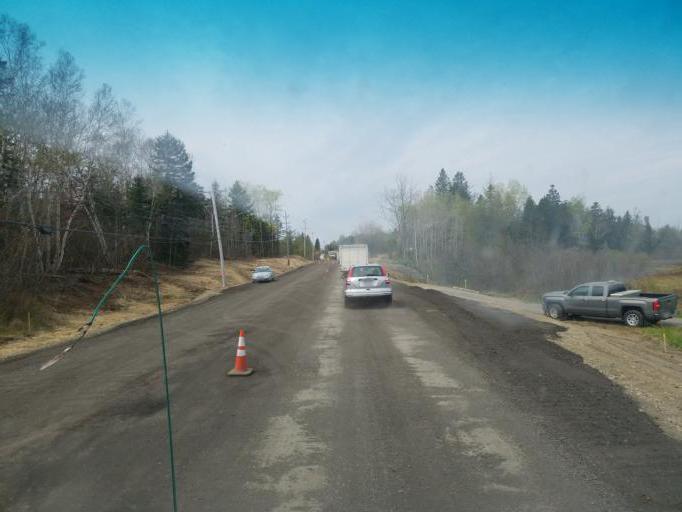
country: US
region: Maine
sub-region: Washington County
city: East Machias
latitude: 44.7656
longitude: -67.2028
